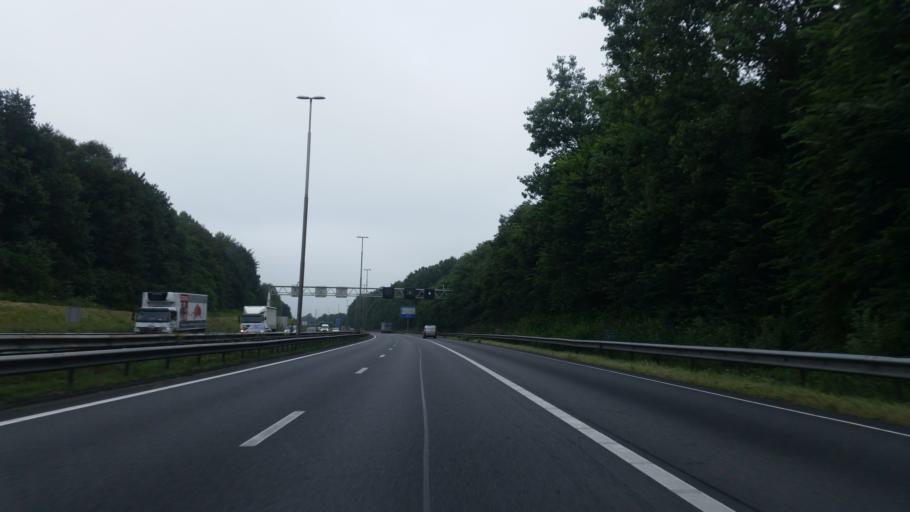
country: NL
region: Limburg
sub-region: Gemeente Stein
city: Berg
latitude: 51.0057
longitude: 5.7931
